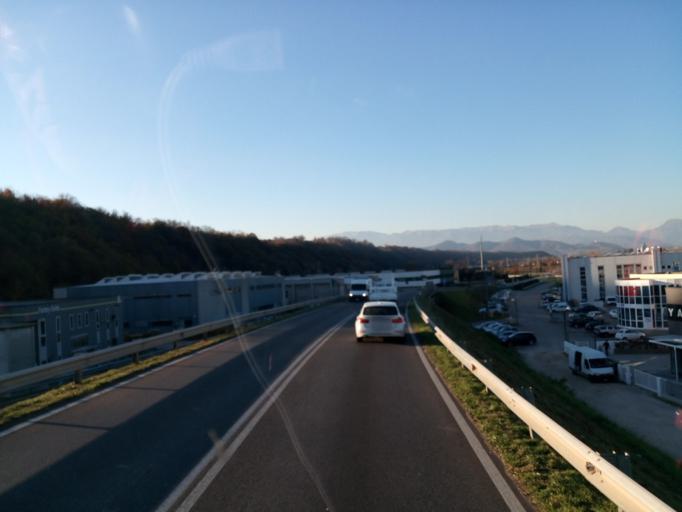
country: IT
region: Veneto
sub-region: Provincia di Treviso
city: Montebelluna
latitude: 45.7837
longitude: 12.0512
